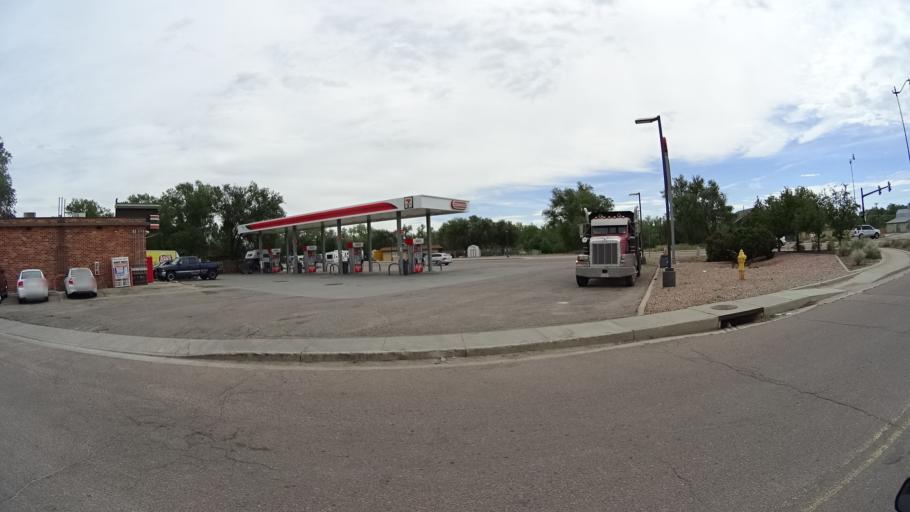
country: US
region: Colorado
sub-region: El Paso County
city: Fountain
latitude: 38.6759
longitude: -104.7064
